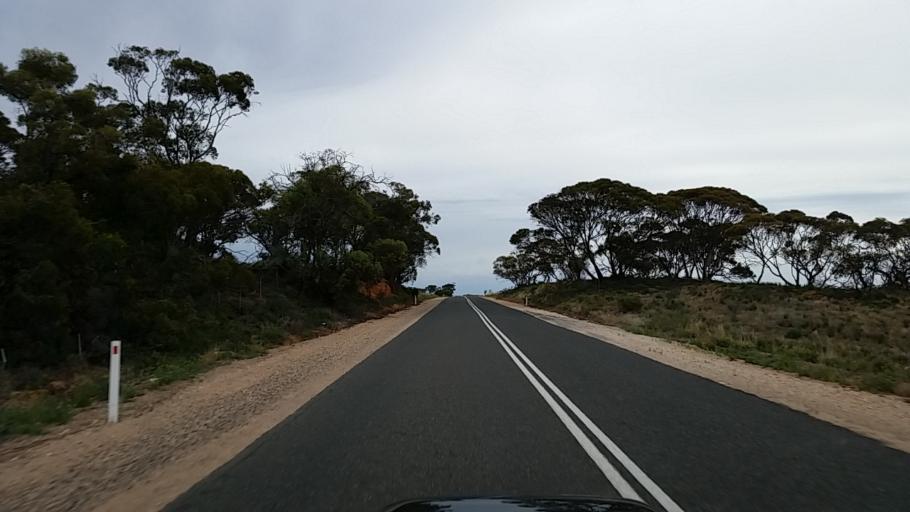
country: AU
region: South Australia
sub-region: Mid Murray
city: Mannum
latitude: -34.7555
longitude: 139.3042
